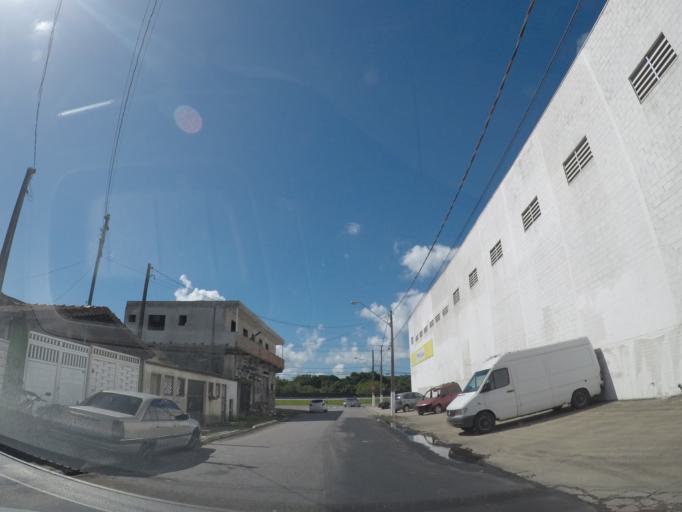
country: BR
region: Sao Paulo
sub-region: Praia Grande
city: Praia Grande
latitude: -24.0253
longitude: -46.5070
